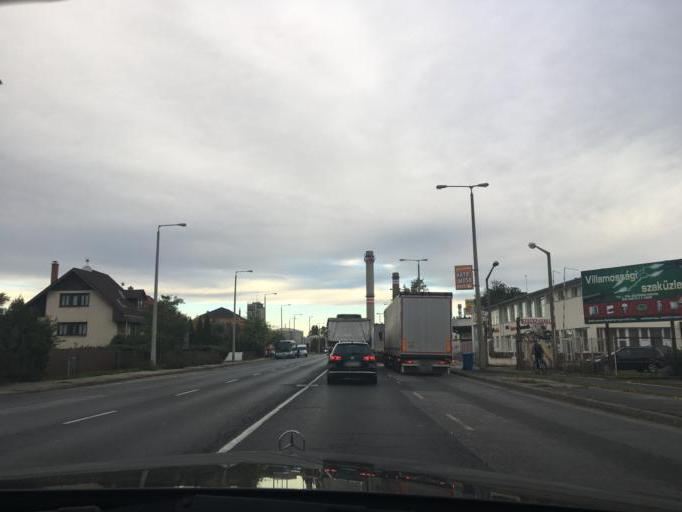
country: HU
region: Hajdu-Bihar
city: Debrecen
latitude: 47.5135
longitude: 21.6295
